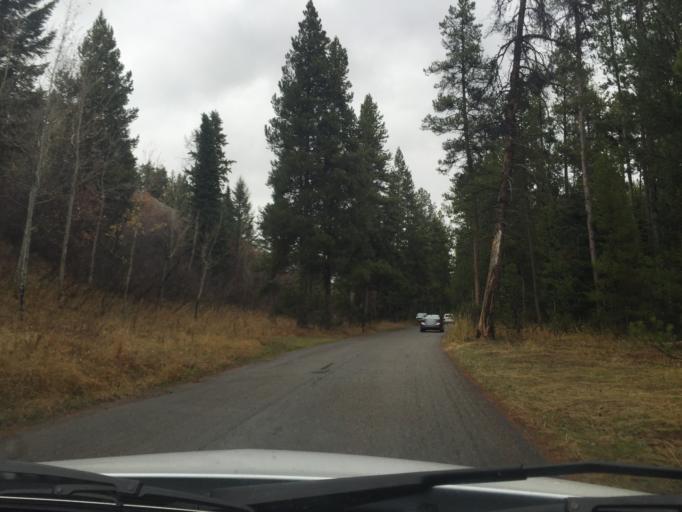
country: US
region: Wyoming
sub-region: Teton County
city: Moose Wilson Road
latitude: 43.6350
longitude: -110.7702
